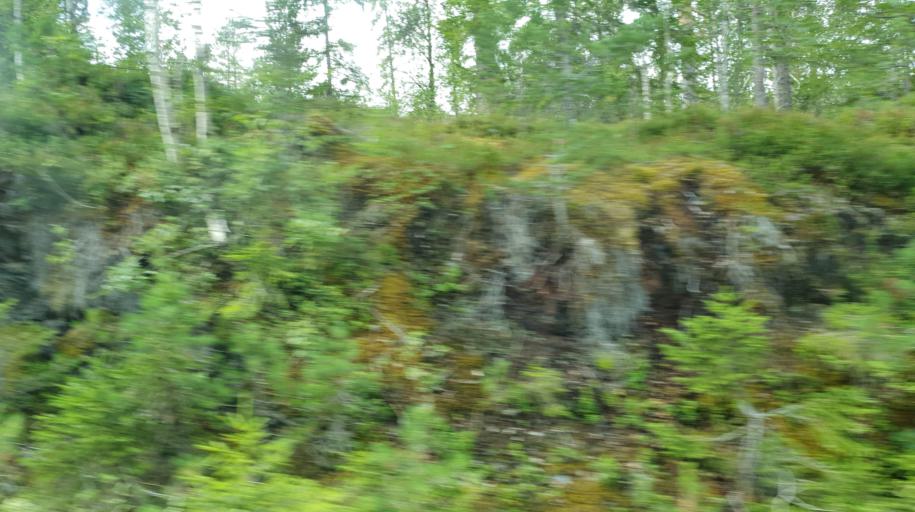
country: NO
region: Nord-Trondelag
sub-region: Levanger
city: Skogn
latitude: 63.5859
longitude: 11.2443
